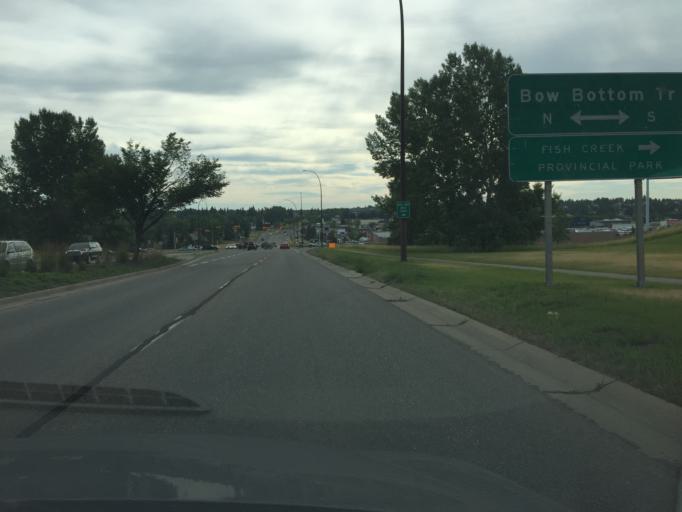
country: CA
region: Alberta
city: Calgary
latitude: 50.9307
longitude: -114.0349
